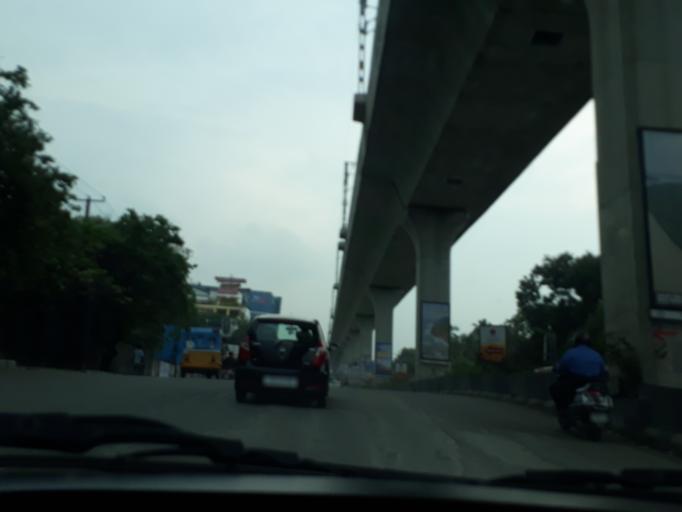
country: IN
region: Telangana
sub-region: Rangareddi
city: Kukatpalli
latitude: 17.4302
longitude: 78.4191
